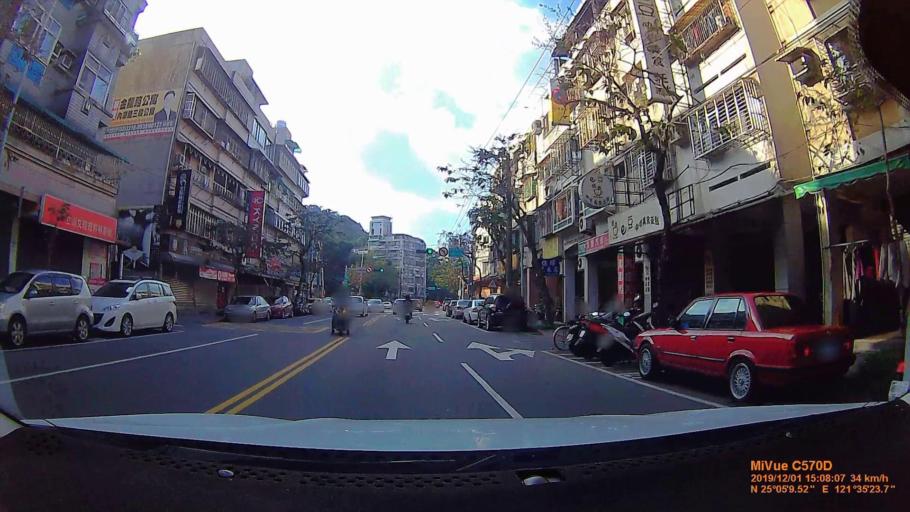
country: TW
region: Taipei
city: Taipei
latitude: 25.0860
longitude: 121.5899
